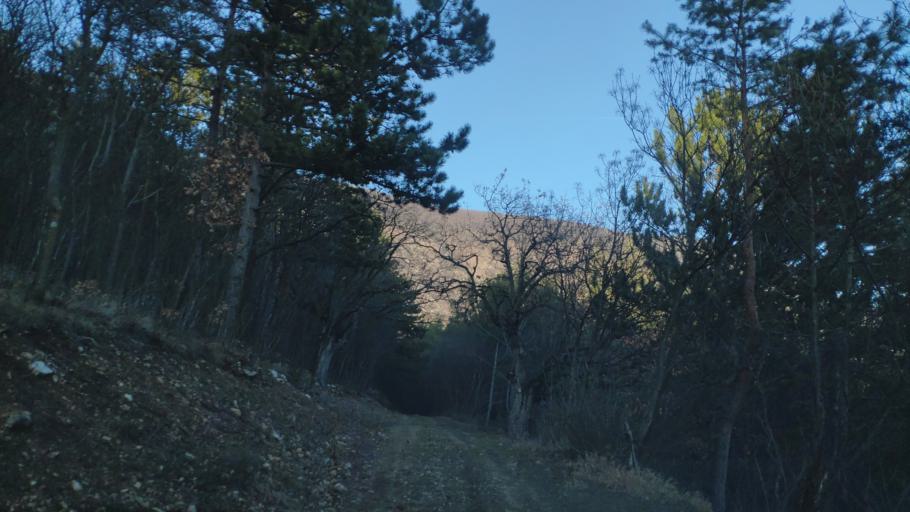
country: SK
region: Kosicky
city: Medzev
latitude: 48.6073
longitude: 20.7379
